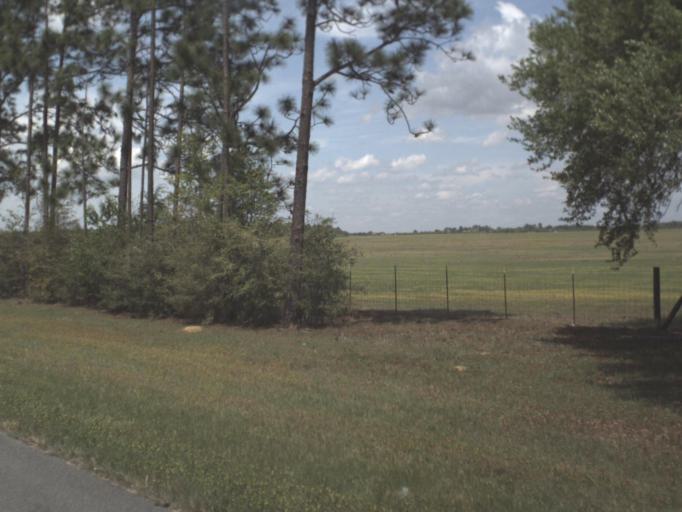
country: US
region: Florida
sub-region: Escambia County
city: Cantonment
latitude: 30.5352
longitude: -87.3615
